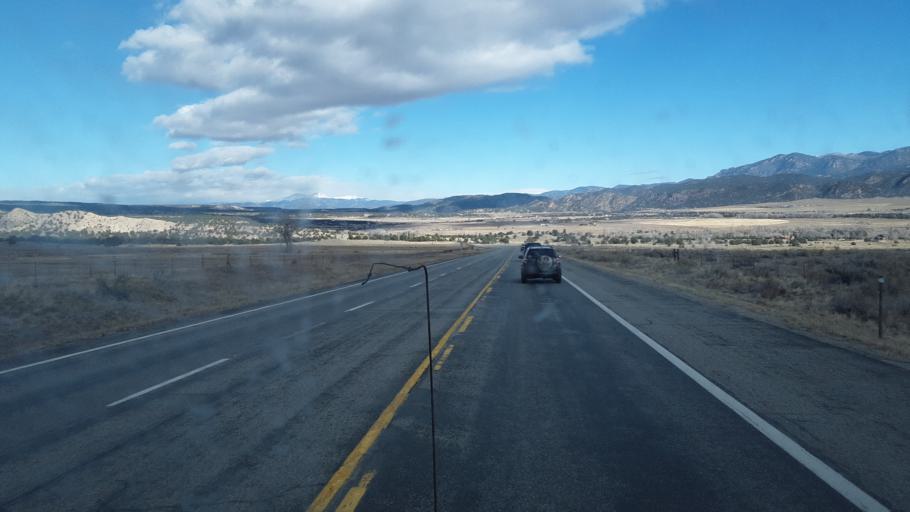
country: US
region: Colorado
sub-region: Chaffee County
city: Salida
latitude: 38.5619
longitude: -106.0810
